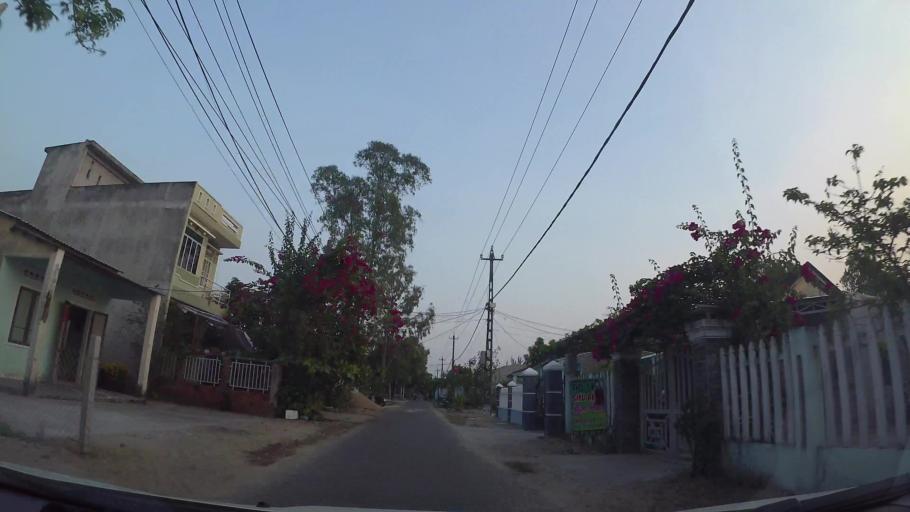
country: VN
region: Da Nang
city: Ngu Hanh Son
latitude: 15.9742
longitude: 108.2398
